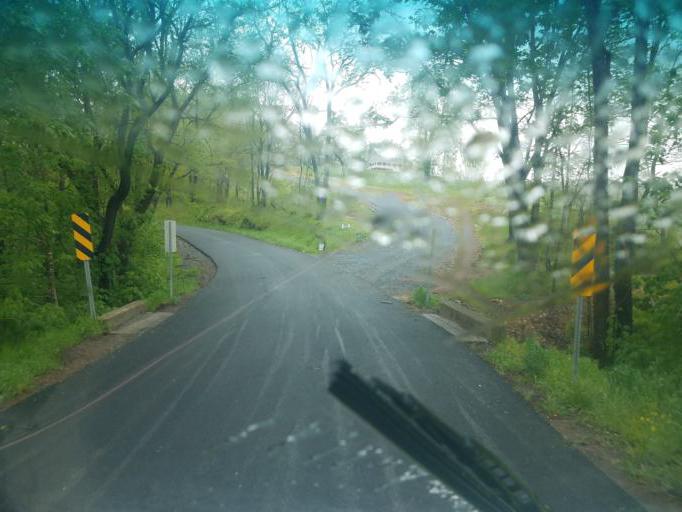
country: US
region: Virginia
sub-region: Smyth County
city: Marion
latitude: 36.9221
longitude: -81.5558
